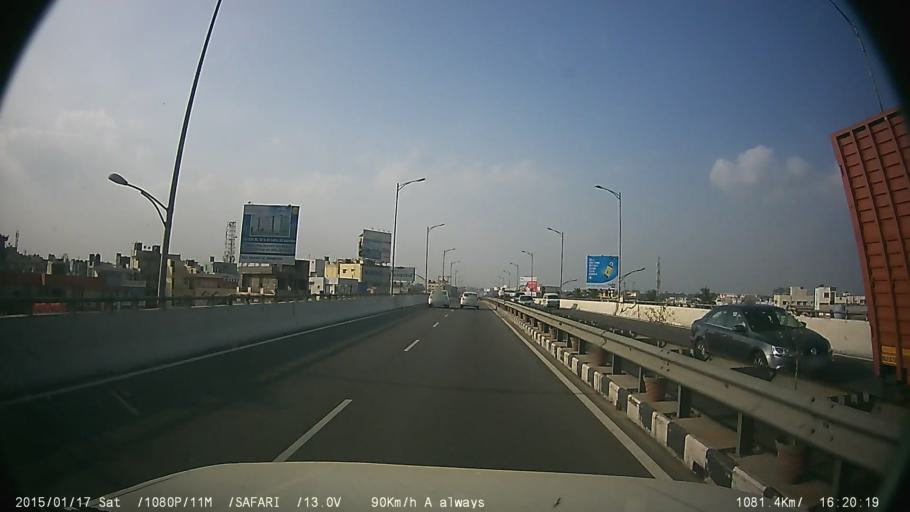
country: IN
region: Karnataka
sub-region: Bangalore Urban
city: Bangalore
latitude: 12.9052
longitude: 77.6303
